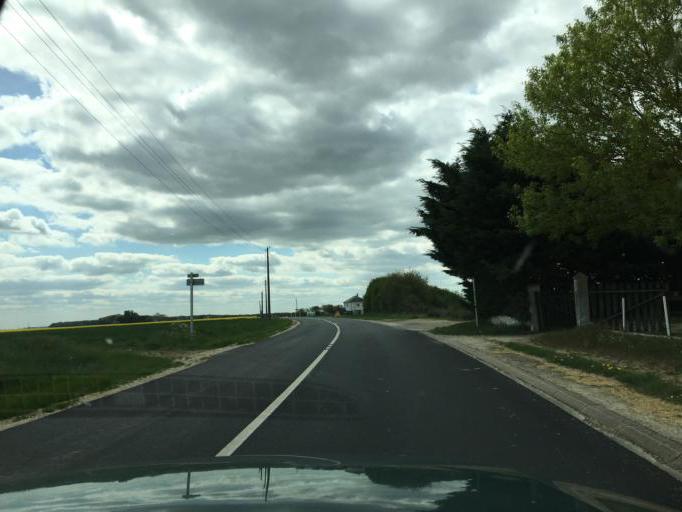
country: FR
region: Centre
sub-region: Departement du Loir-et-Cher
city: Oucques
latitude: 47.8069
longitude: 1.2487
